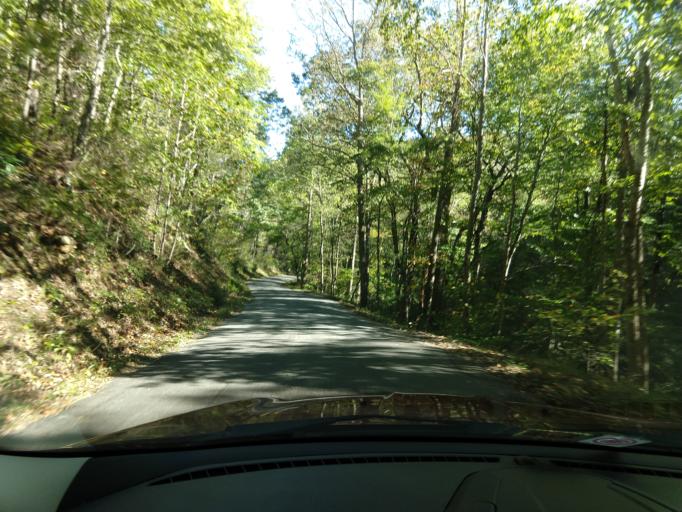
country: US
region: Virginia
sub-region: Alleghany County
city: Clifton Forge
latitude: 37.8590
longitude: -79.8763
